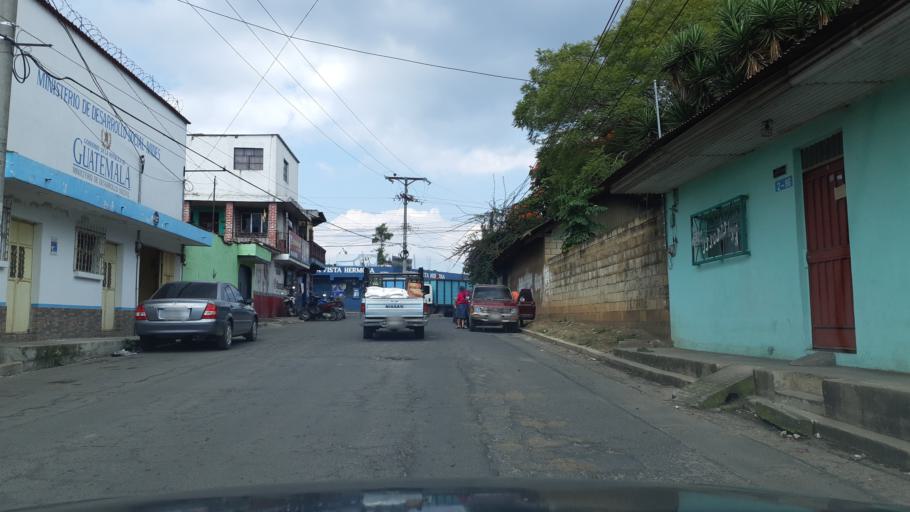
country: GT
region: Chimaltenango
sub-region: Municipio de Chimaltenango
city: Chimaltenango
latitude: 14.6627
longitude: -90.8263
